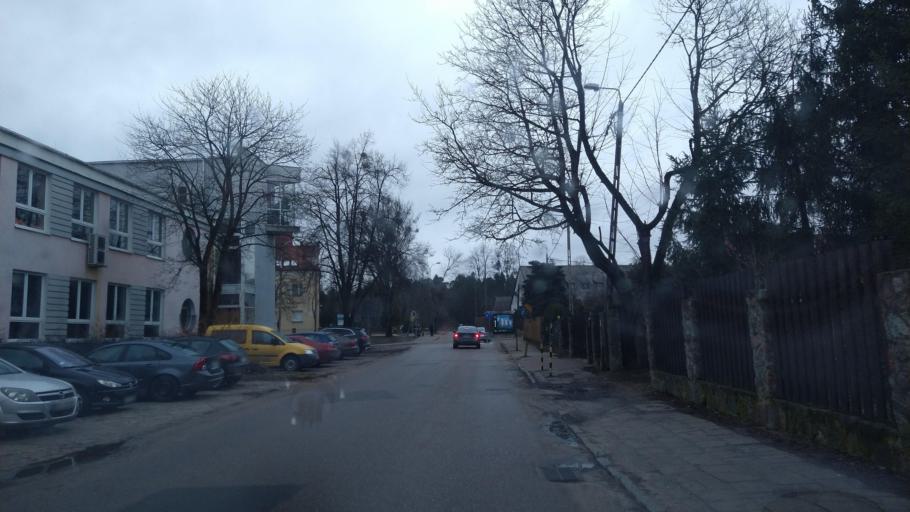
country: PL
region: Warmian-Masurian Voivodeship
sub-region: Powiat olsztynski
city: Olsztyn
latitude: 53.7978
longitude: 20.4950
